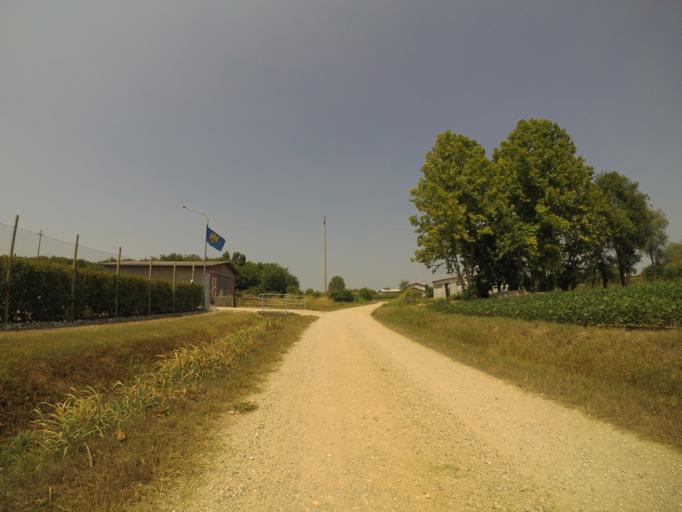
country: IT
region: Friuli Venezia Giulia
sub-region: Provincia di Udine
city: Talmassons
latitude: 45.9223
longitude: 13.1227
